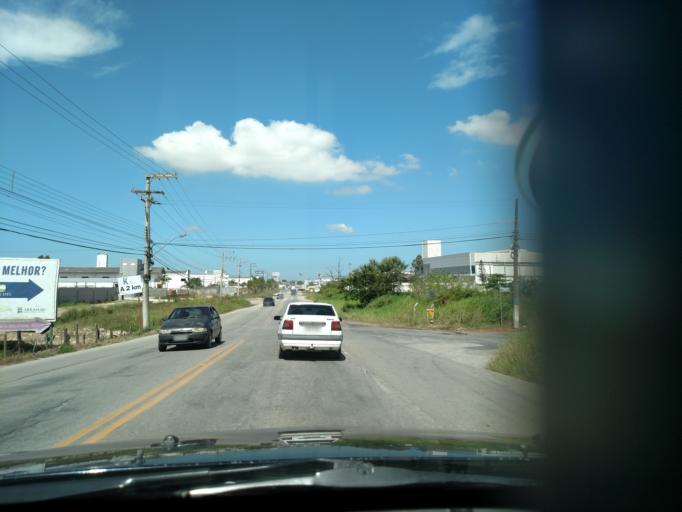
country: BR
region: Santa Catarina
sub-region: Itajai
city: Itajai
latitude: -26.8867
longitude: -48.7382
